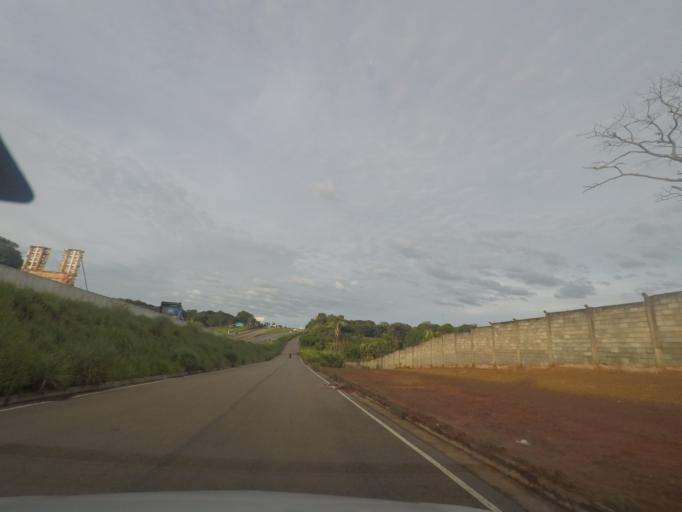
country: BR
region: Goias
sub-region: Trindade
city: Trindade
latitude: -16.7352
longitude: -49.4029
